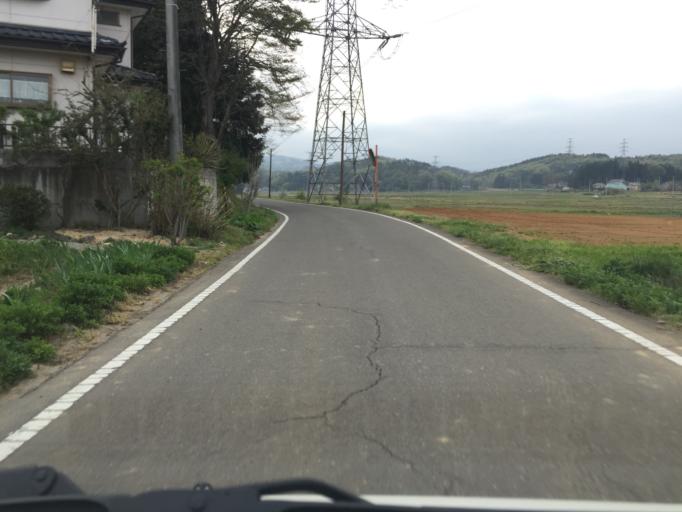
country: JP
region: Fukushima
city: Nihommatsu
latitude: 37.6470
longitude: 140.4498
